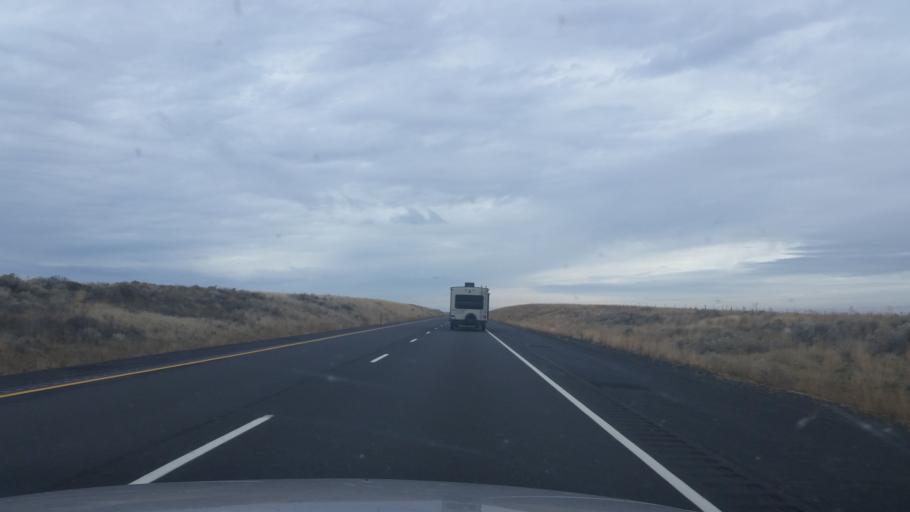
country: US
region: Washington
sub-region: Adams County
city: Ritzville
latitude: 47.0929
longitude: -118.6975
